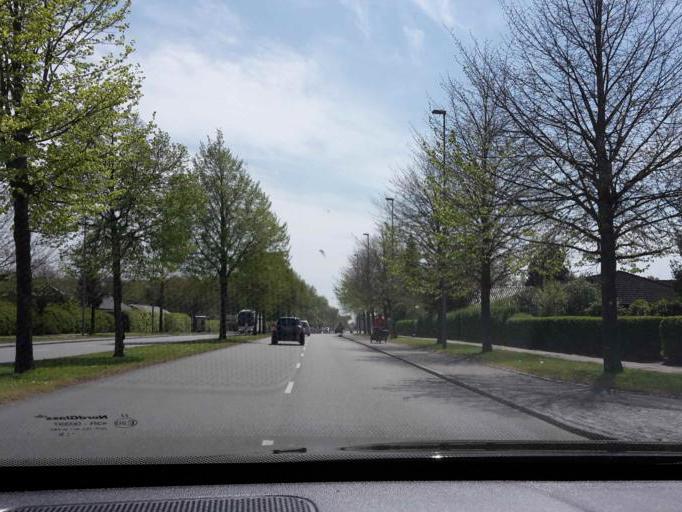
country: DK
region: South Denmark
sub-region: Odense Kommune
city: Odense
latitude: 55.3763
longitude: 10.4088
